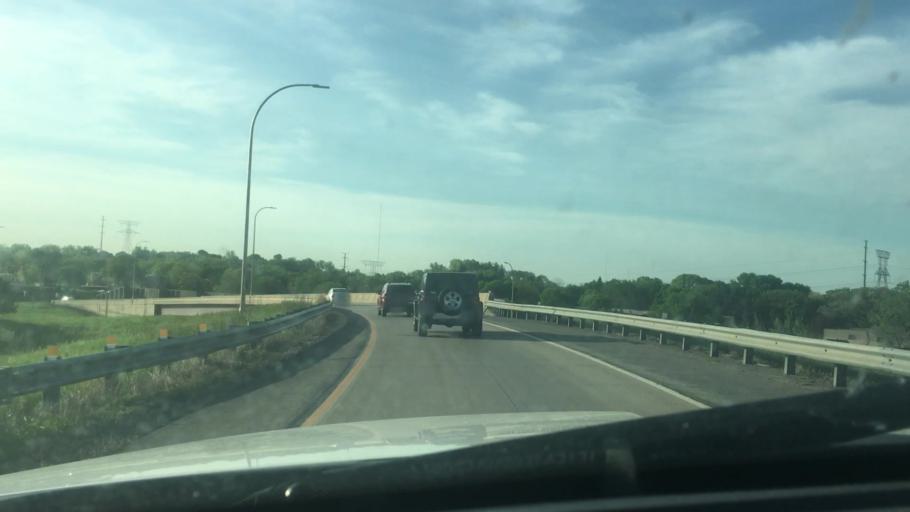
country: US
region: Minnesota
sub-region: Ramsey County
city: Vadnais Heights
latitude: 45.0381
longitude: -93.0622
